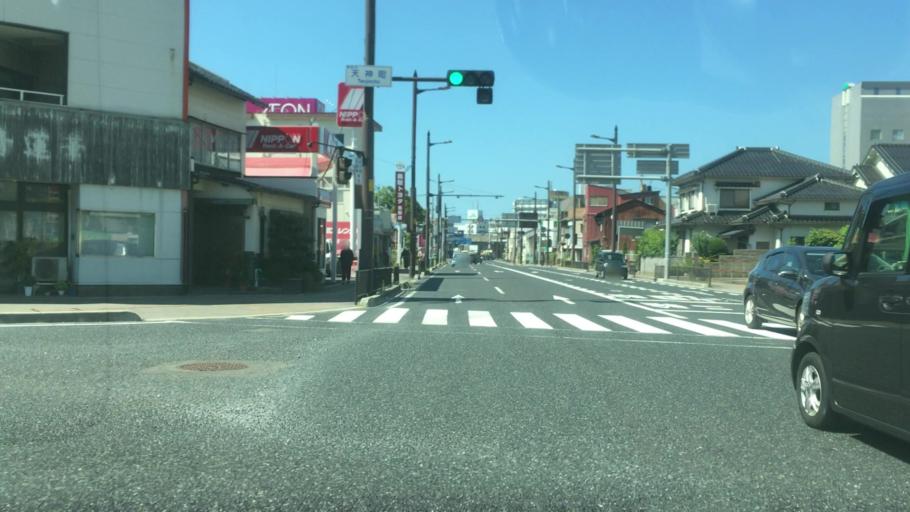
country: JP
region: Tottori
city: Tottori
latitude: 35.4918
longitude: 134.2229
